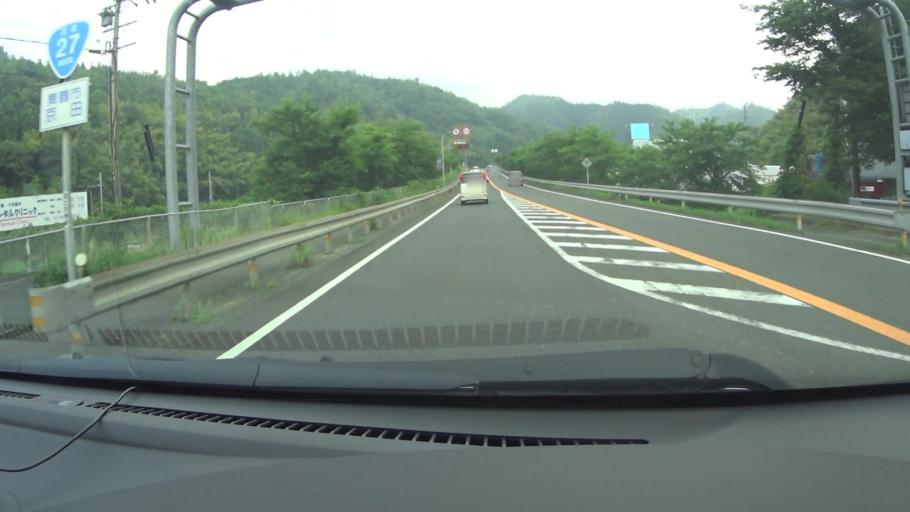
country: JP
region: Kyoto
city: Maizuru
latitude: 35.4177
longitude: 135.3314
